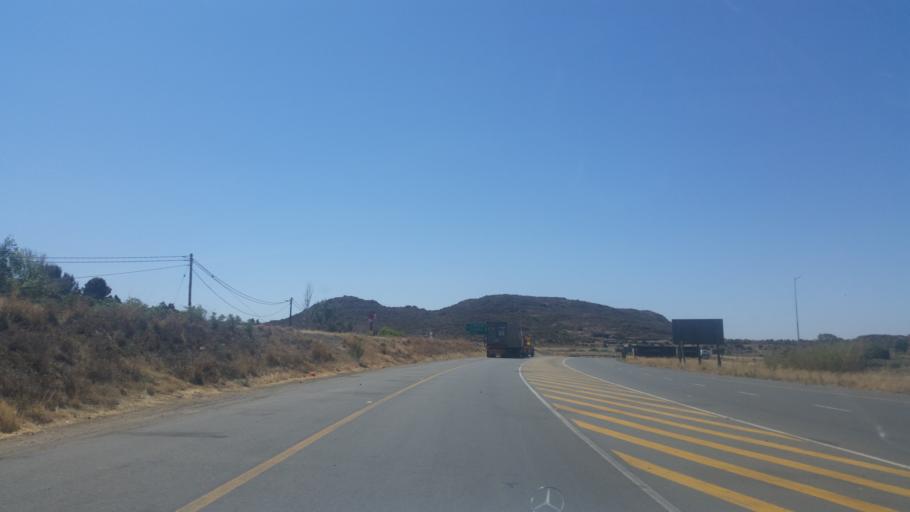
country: ZA
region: Northern Cape
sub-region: Pixley ka Seme District Municipality
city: Colesberg
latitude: -30.7268
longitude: 25.0832
